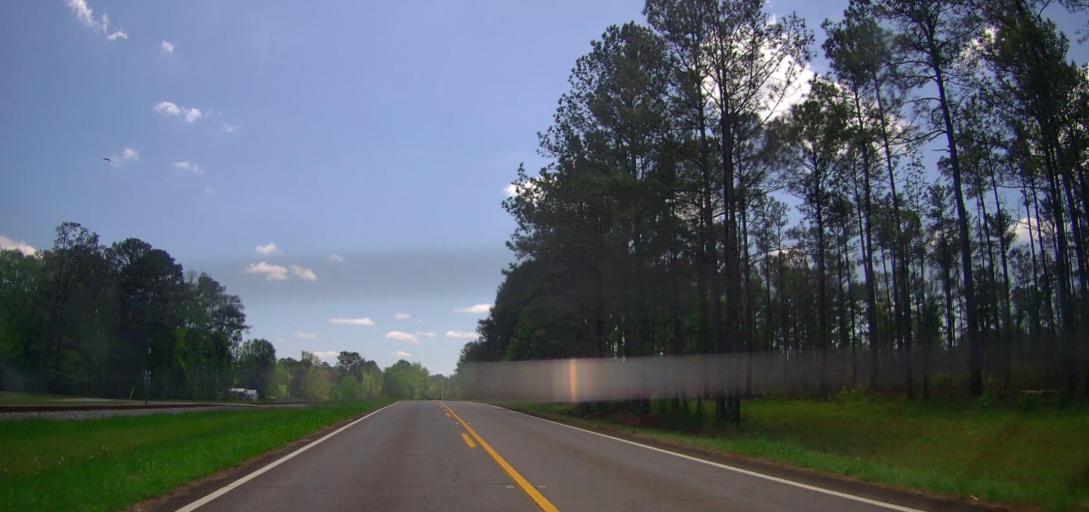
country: US
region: Georgia
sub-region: Jones County
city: Gray
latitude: 33.1223
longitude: -83.6267
